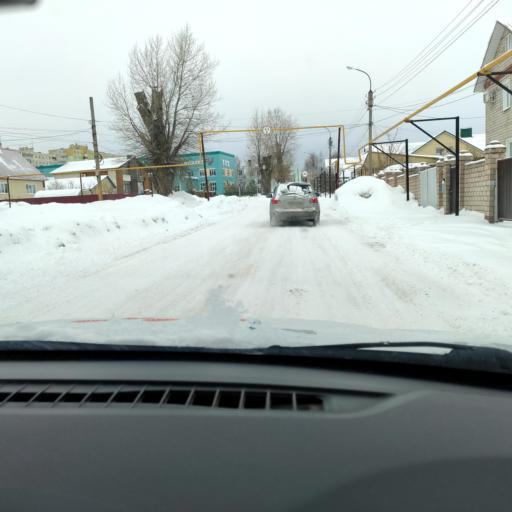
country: RU
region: Bashkortostan
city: Blagoveshchensk
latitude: 55.0477
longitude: 55.9651
